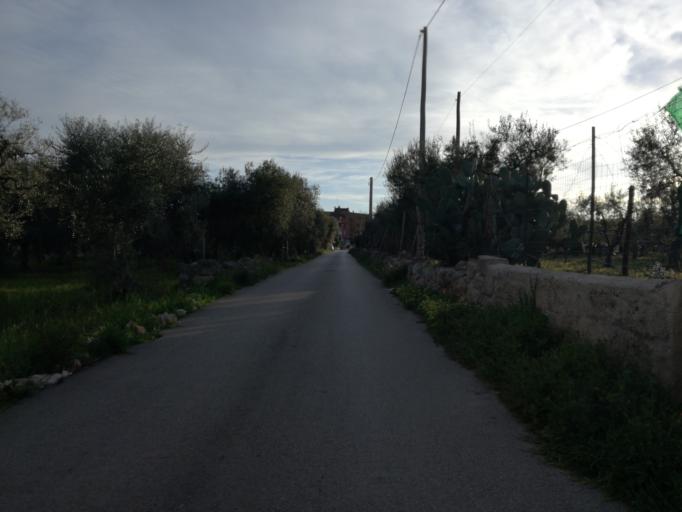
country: IT
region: Apulia
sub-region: Provincia di Bari
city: Valenzano
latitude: 41.0490
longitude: 16.8902
